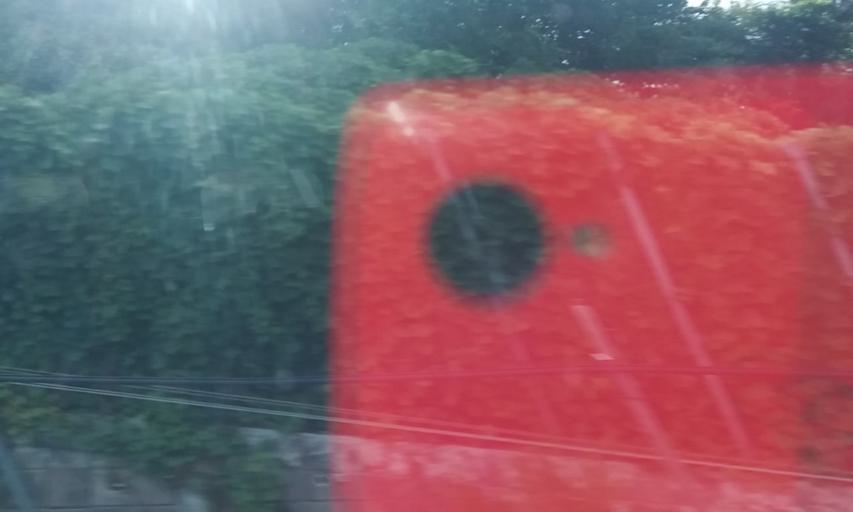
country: JP
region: Fukushima
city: Sukagawa
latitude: 37.3372
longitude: 140.3657
